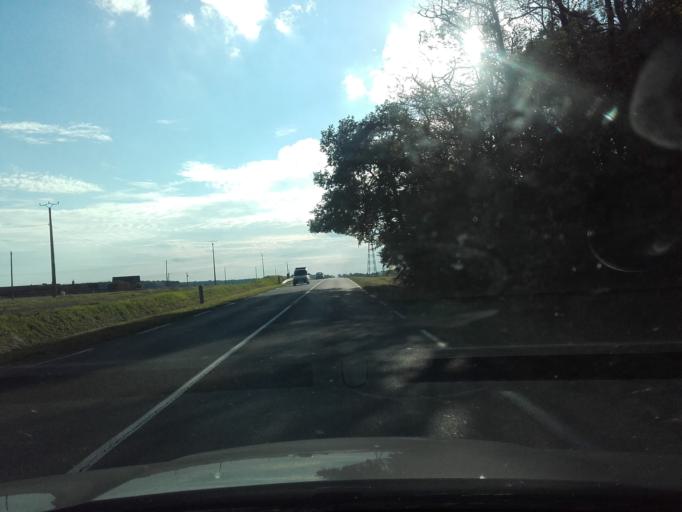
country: FR
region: Centre
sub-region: Departement d'Indre-et-Loire
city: Monnaie
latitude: 47.4824
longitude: 0.7662
